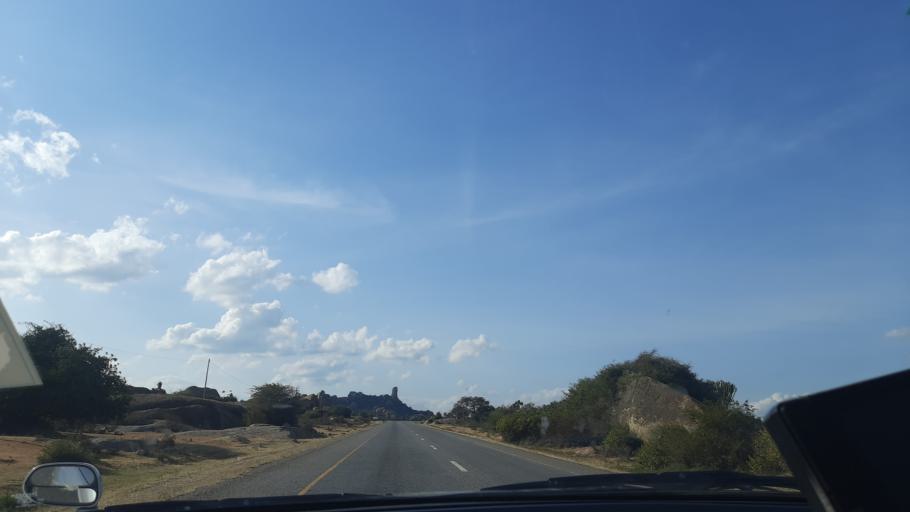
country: TZ
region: Singida
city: Puma
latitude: -4.9861
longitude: 34.7558
